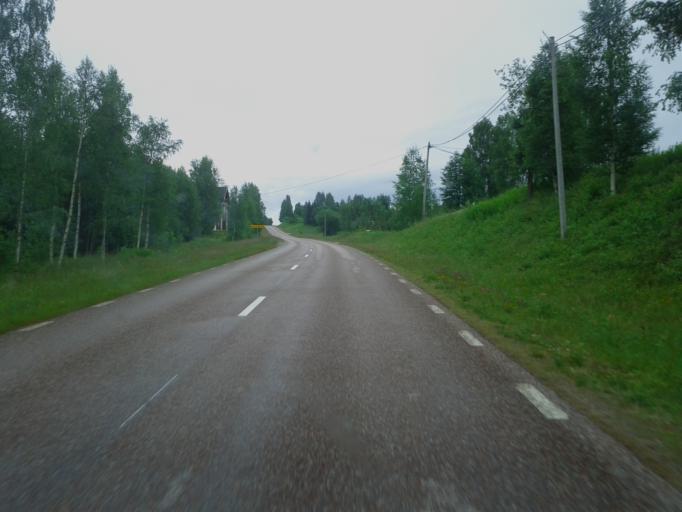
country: NO
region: Hedmark
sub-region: Trysil
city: Innbygda
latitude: 61.7357
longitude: 12.9811
